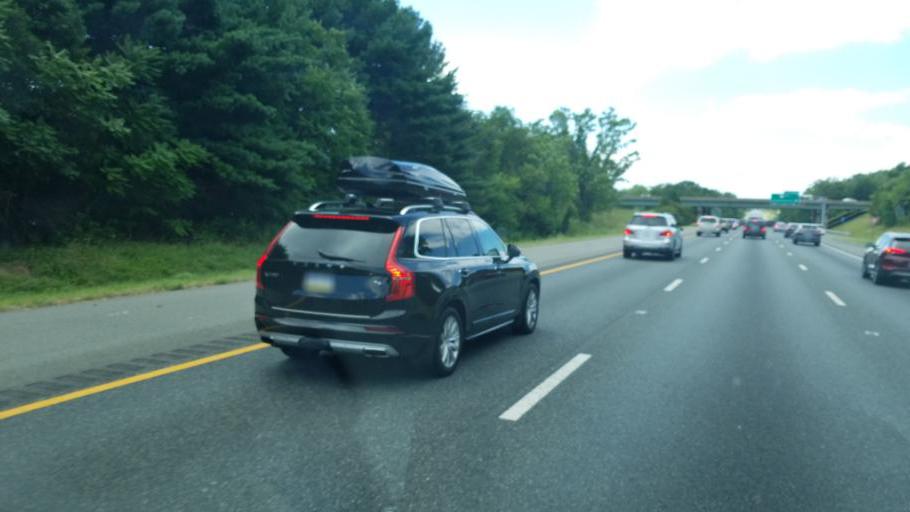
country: US
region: Virginia
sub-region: Stafford County
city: Falmouth
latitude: 38.2985
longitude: -77.5051
